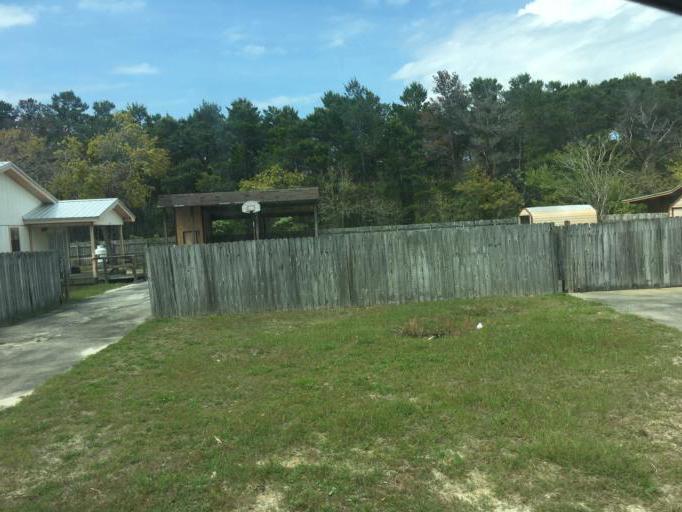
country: US
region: Florida
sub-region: Bay County
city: Laguna Beach
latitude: 30.2357
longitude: -85.8924
